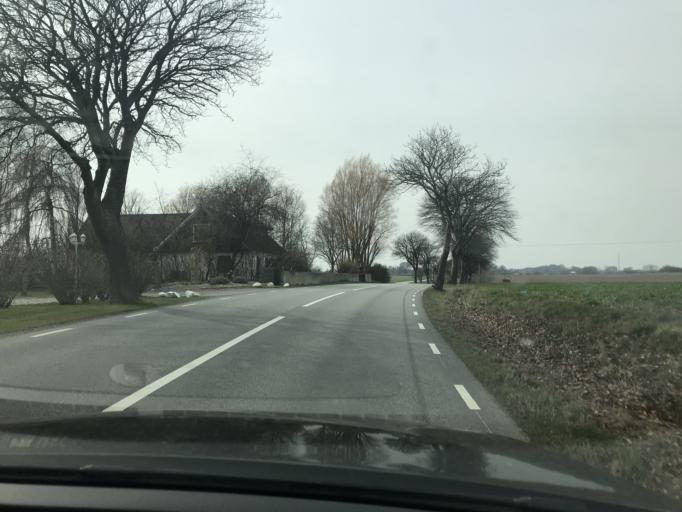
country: SE
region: Skane
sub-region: Skurups Kommun
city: Skivarp
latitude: 55.4238
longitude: 13.5998
